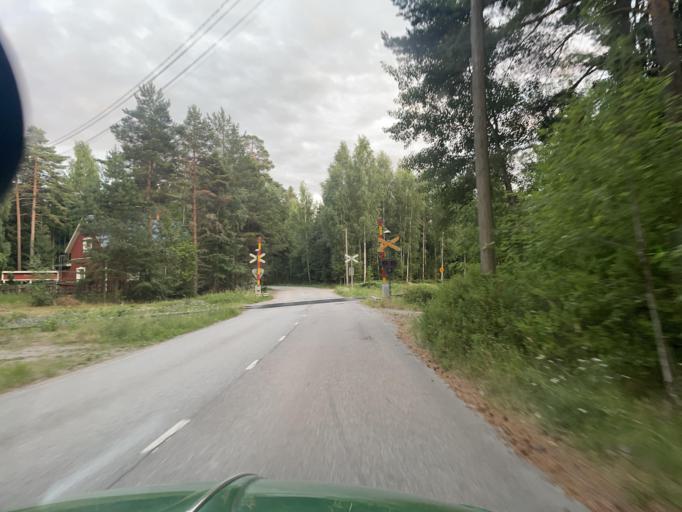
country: FI
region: Uusimaa
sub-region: Helsinki
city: Lohja
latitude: 60.2350
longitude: 24.0690
